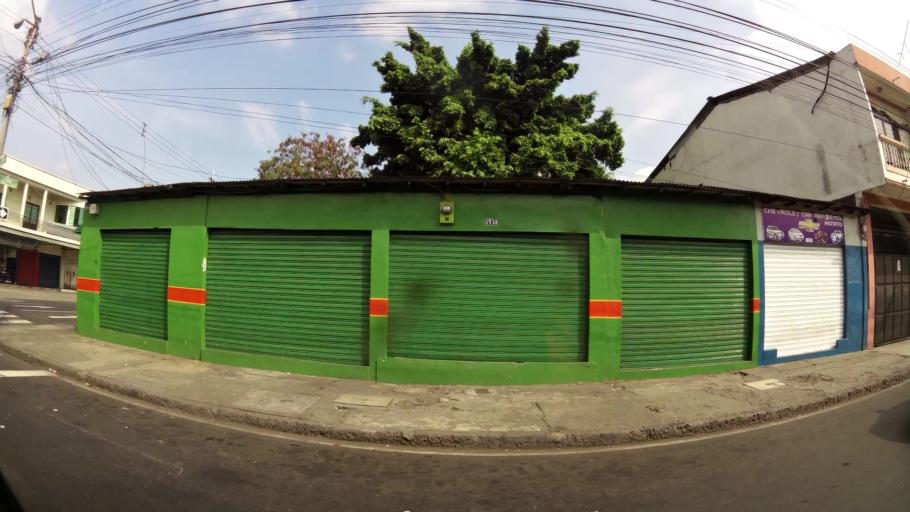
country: EC
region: Guayas
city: Guayaquil
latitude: -2.1956
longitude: -79.8989
